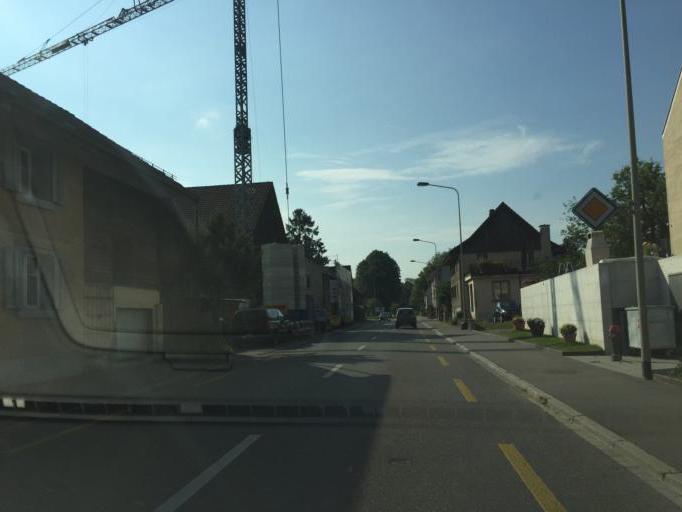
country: CH
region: Zurich
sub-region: Bezirk Buelach
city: Rorbas
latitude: 47.5303
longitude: 8.5750
